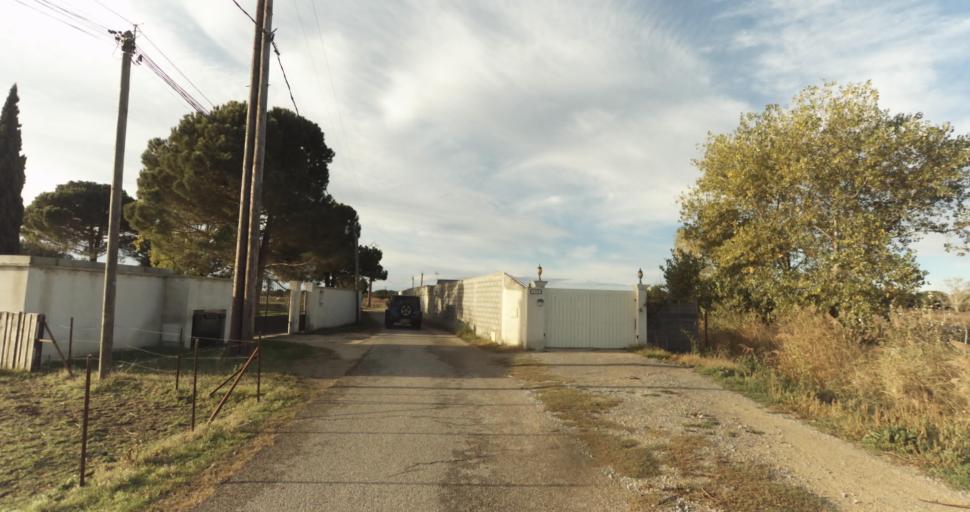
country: FR
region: Languedoc-Roussillon
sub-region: Departement du Gard
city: Aigues-Mortes
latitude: 43.5579
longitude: 4.2134
